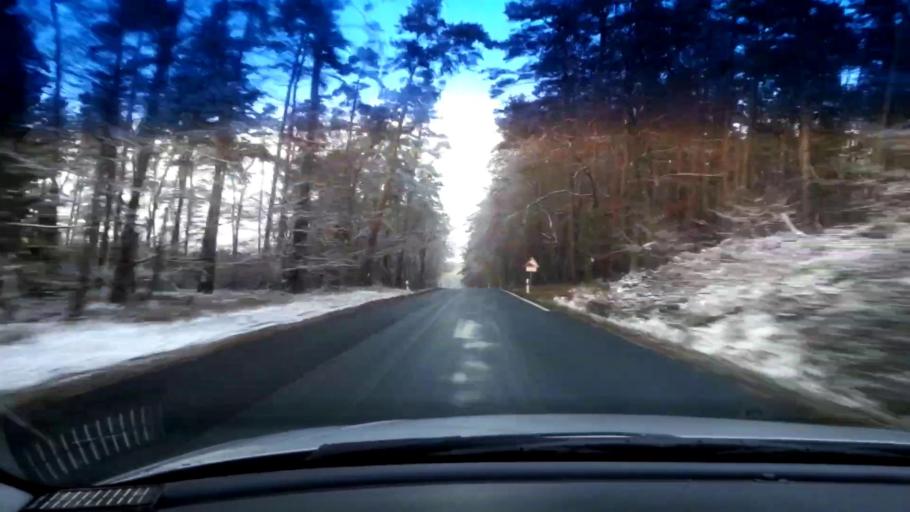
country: DE
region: Bavaria
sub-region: Regierungsbezirk Mittelfranken
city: Adelsdorf
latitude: 49.7656
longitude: 10.8937
